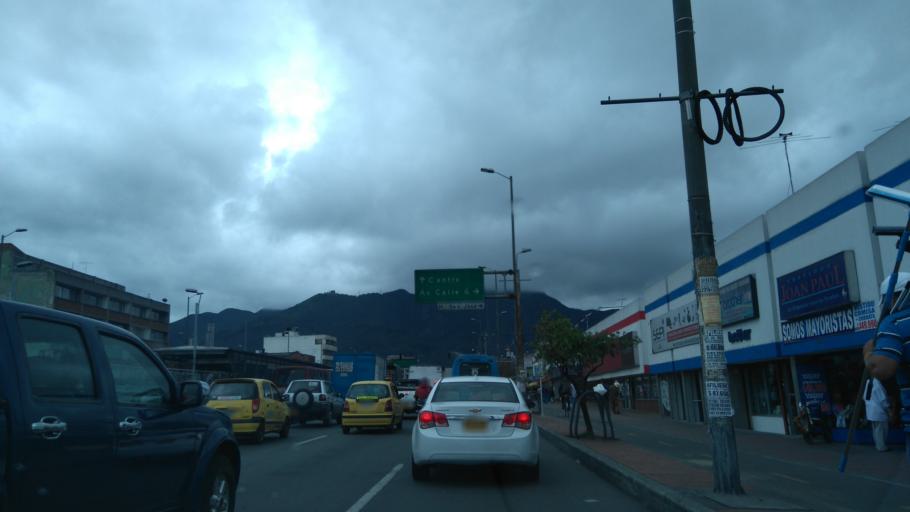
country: CO
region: Bogota D.C.
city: Bogota
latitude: 4.6126
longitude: -74.0902
